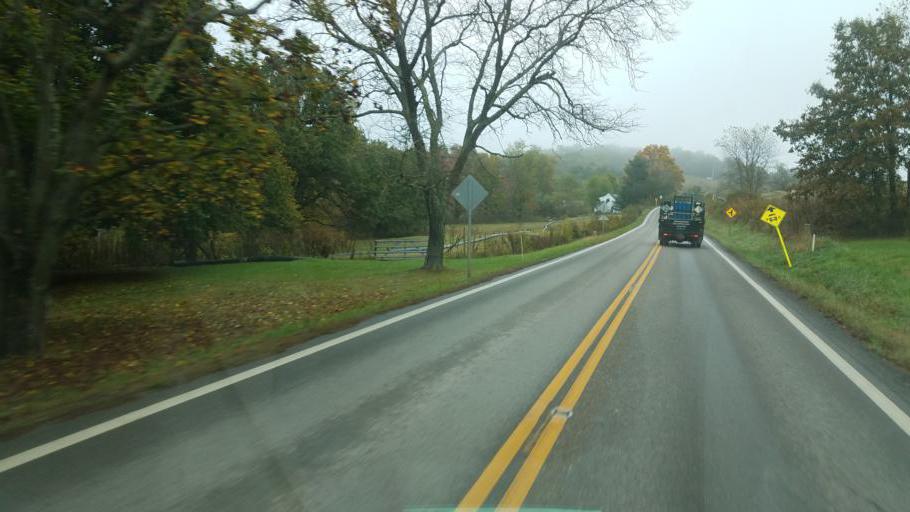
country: US
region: Ohio
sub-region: Carroll County
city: Carrollton
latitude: 40.4162
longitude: -81.1329
